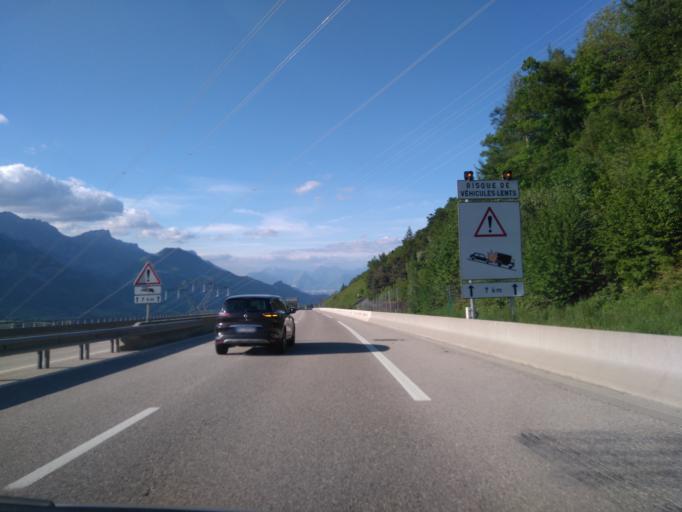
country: FR
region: Rhone-Alpes
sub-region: Departement de l'Isere
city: Le Gua
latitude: 44.9786
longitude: 5.6461
